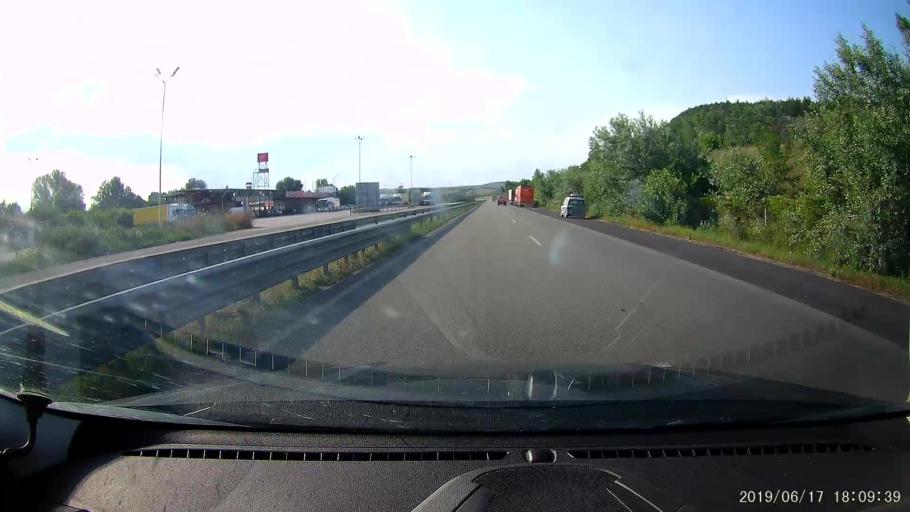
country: BG
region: Khaskovo
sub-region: Obshtina Lyubimets
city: Lyubimets
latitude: 41.8629
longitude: 26.0874
